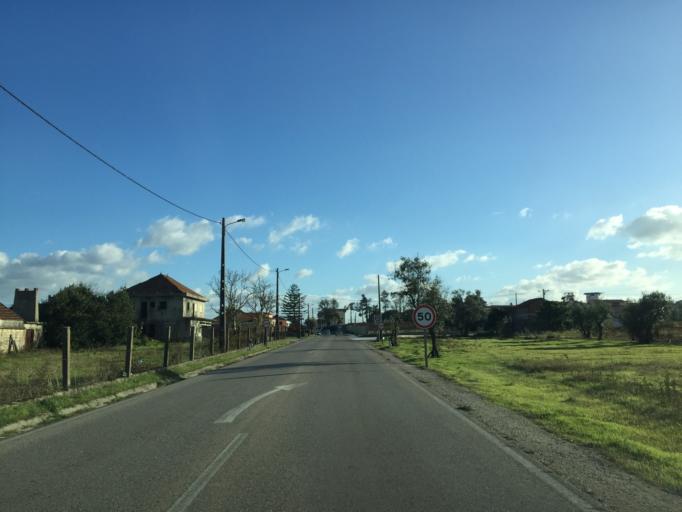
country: PT
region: Leiria
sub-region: Pombal
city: Lourical
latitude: 39.9554
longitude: -8.7864
